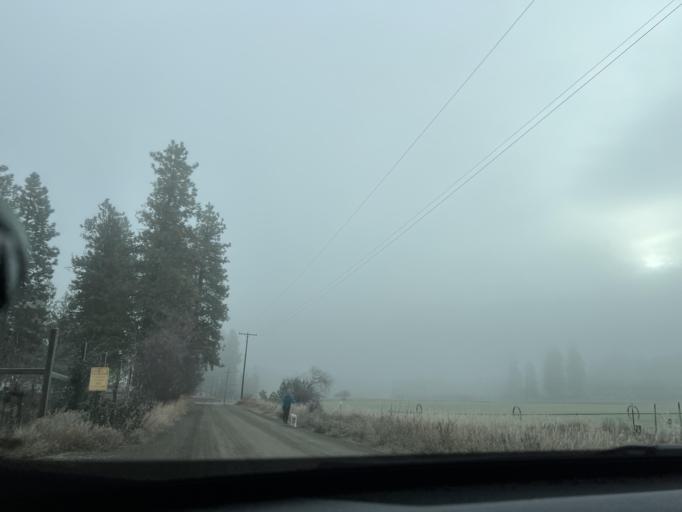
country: US
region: Washington
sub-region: Okanogan County
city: Brewster
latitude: 48.4616
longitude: -120.2093
